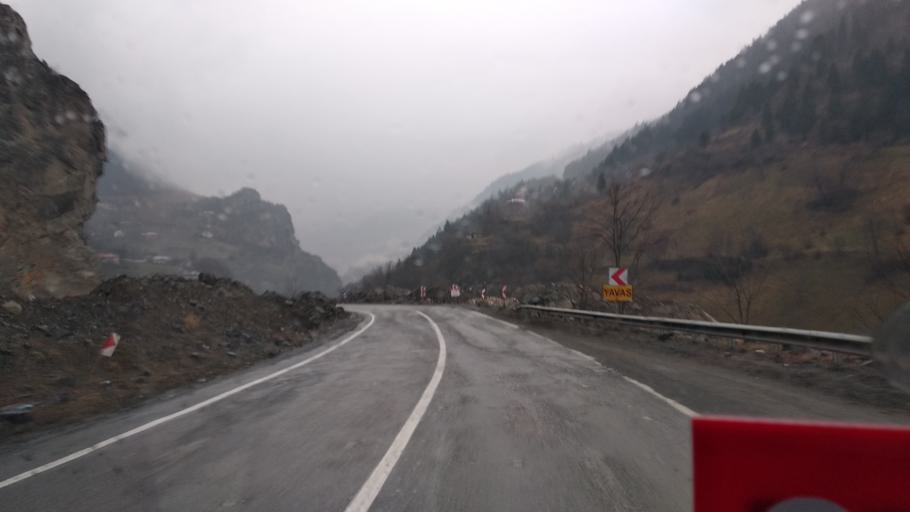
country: TR
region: Trabzon
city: Macka
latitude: 40.7241
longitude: 39.5219
